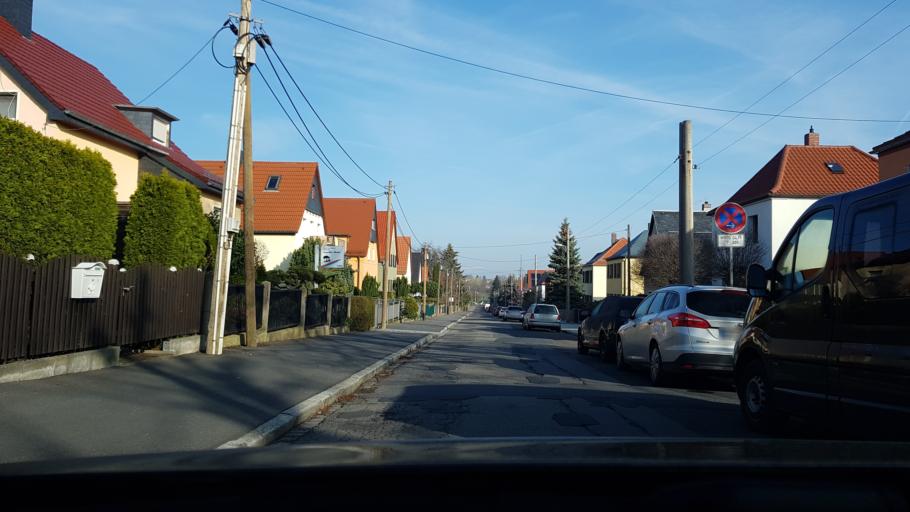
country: DE
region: Saxony
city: Kreischa
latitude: 50.9983
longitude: 13.7869
